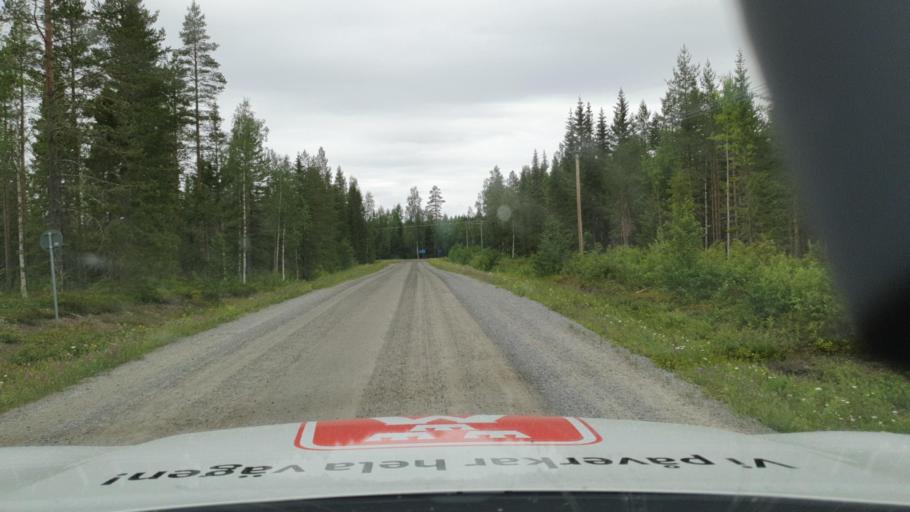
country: SE
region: Vaesterbotten
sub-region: Nordmalings Kommun
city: Nordmaling
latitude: 63.7646
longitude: 19.4785
